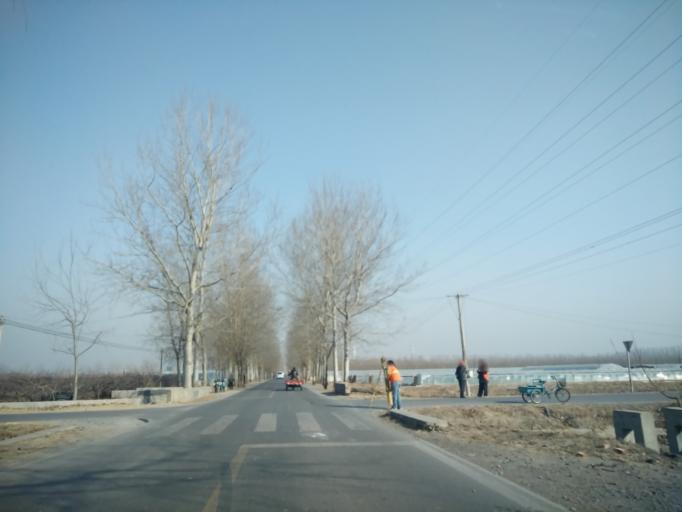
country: CN
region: Beijing
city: Qingyundian
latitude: 39.6907
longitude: 116.4605
